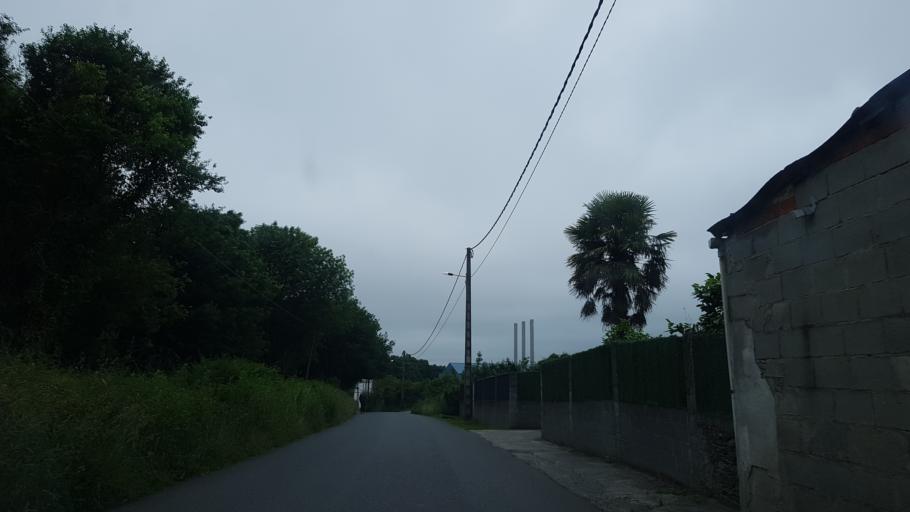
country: ES
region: Galicia
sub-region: Provincia de Lugo
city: Lugo
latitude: 43.0456
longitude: -7.5809
